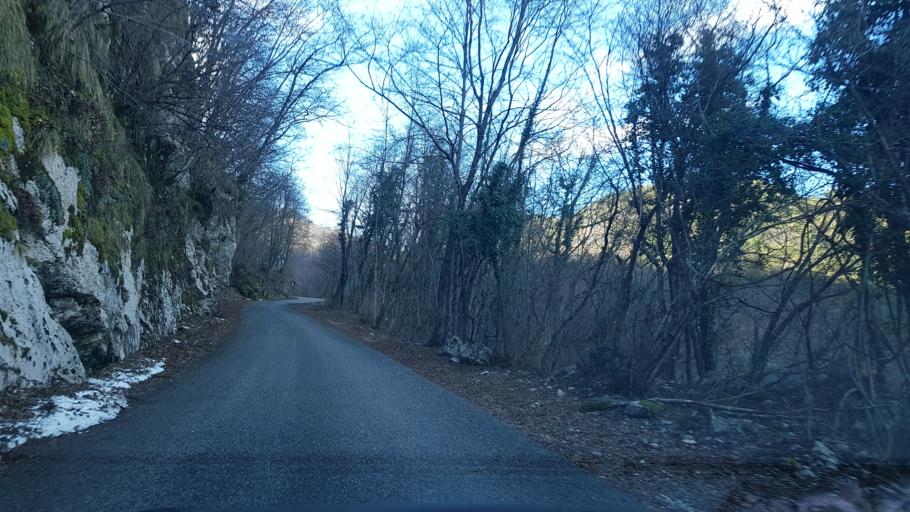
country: IT
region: Friuli Venezia Giulia
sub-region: Provincia di Udine
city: Trasaghis
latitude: 46.2900
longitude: 13.0371
